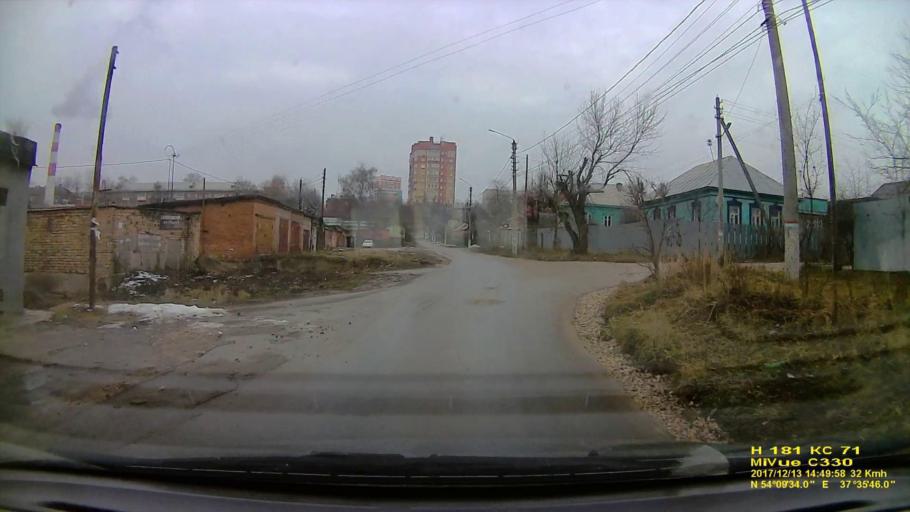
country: RU
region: Tula
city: Mendeleyevskiy
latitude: 54.1595
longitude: 37.5960
